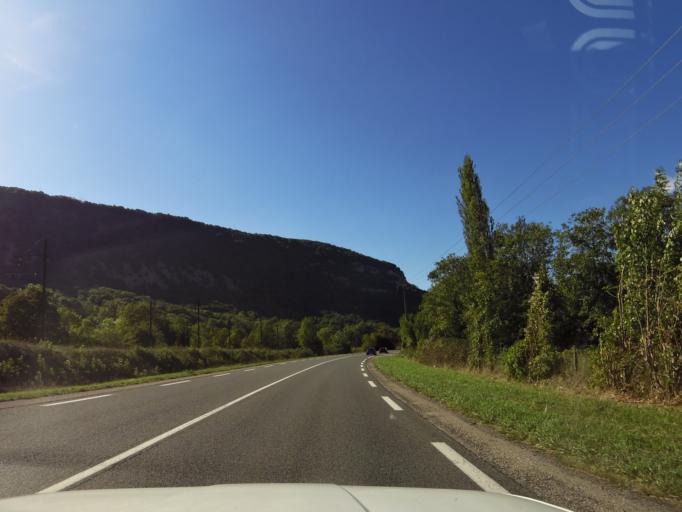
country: FR
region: Rhone-Alpes
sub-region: Departement de l'Ain
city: Saint-Sorlin-en-Bugey
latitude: 45.9188
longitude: 5.3965
